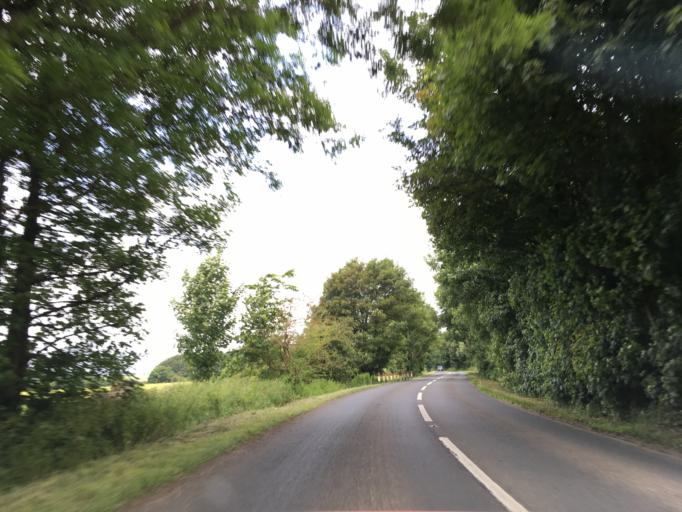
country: GB
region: England
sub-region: Gloucestershire
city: Nailsworth
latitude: 51.6588
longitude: -2.2644
